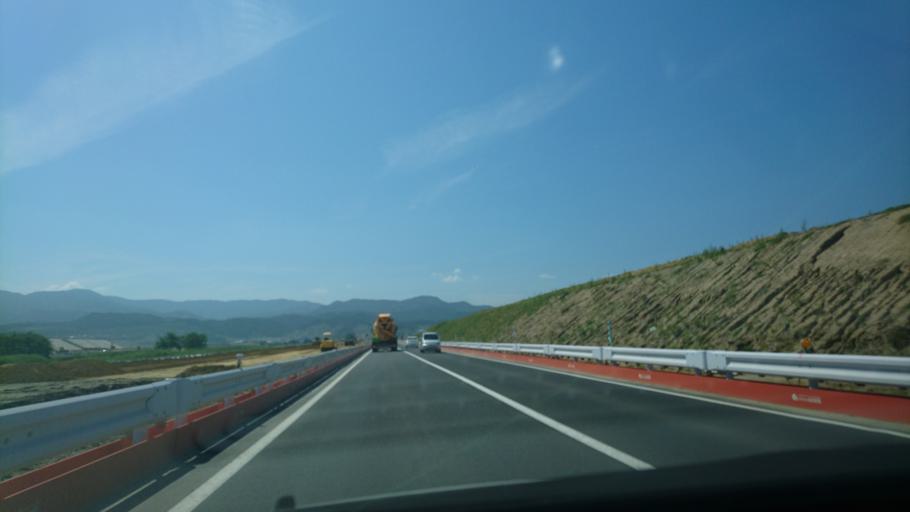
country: JP
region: Iwate
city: Ofunato
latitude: 39.0096
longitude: 141.6422
